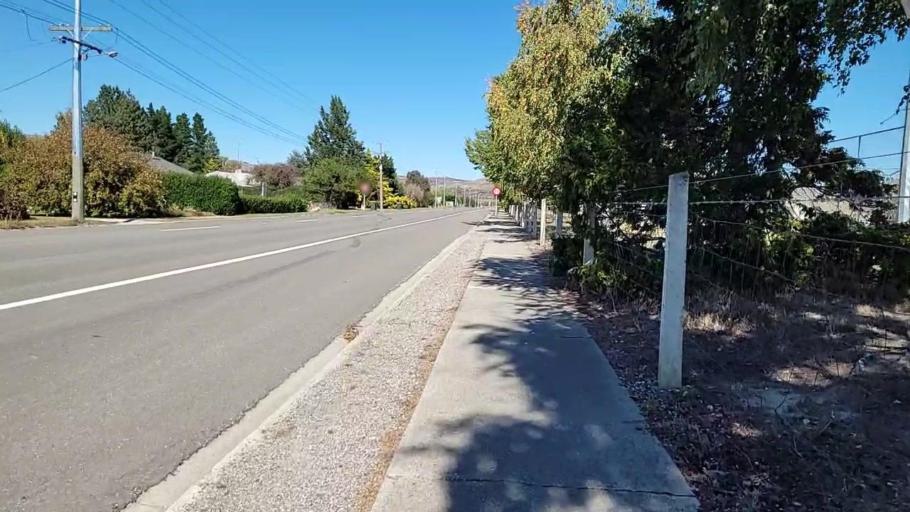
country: NZ
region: Otago
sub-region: Queenstown-Lakes District
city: Wanaka
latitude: -45.1000
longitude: 169.5969
